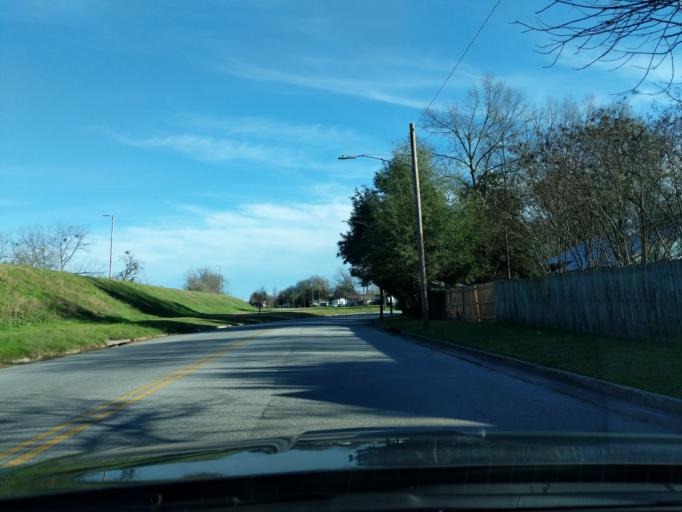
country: US
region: Georgia
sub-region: Richmond County
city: Augusta
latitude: 33.4730
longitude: -81.9537
